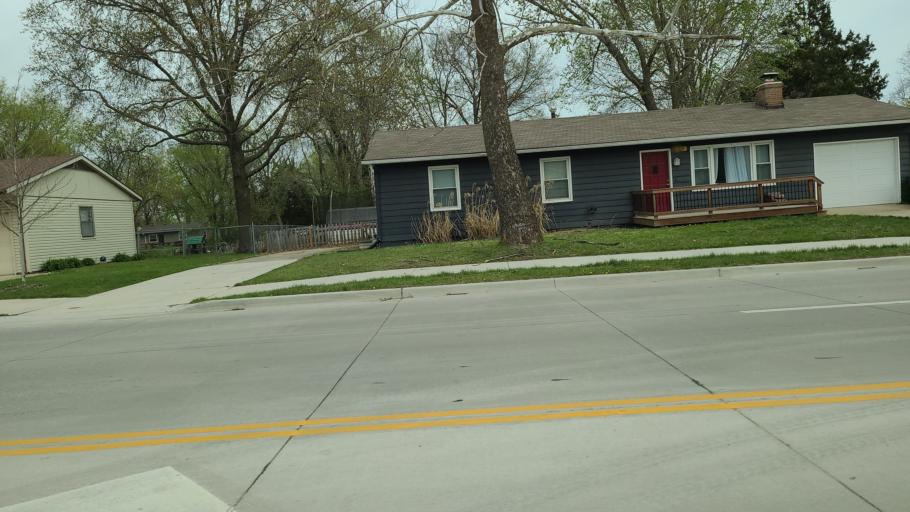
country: US
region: Kansas
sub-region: Douglas County
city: Lawrence
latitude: 38.9698
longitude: -95.2813
